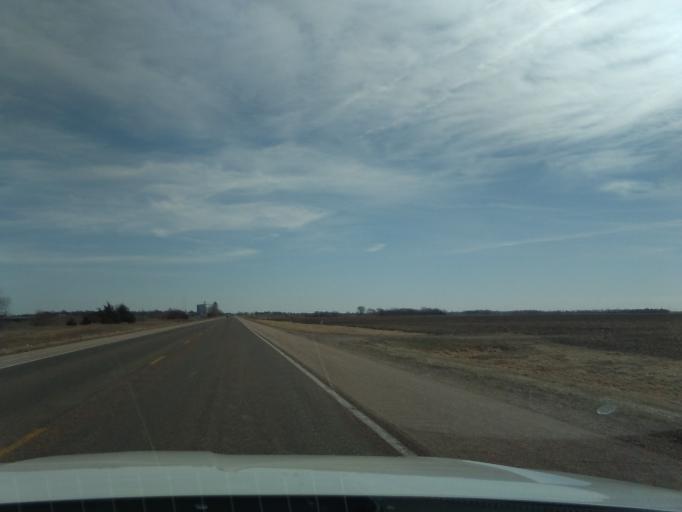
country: US
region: Nebraska
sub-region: Saline County
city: Friend
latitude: 40.6522
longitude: -97.1485
